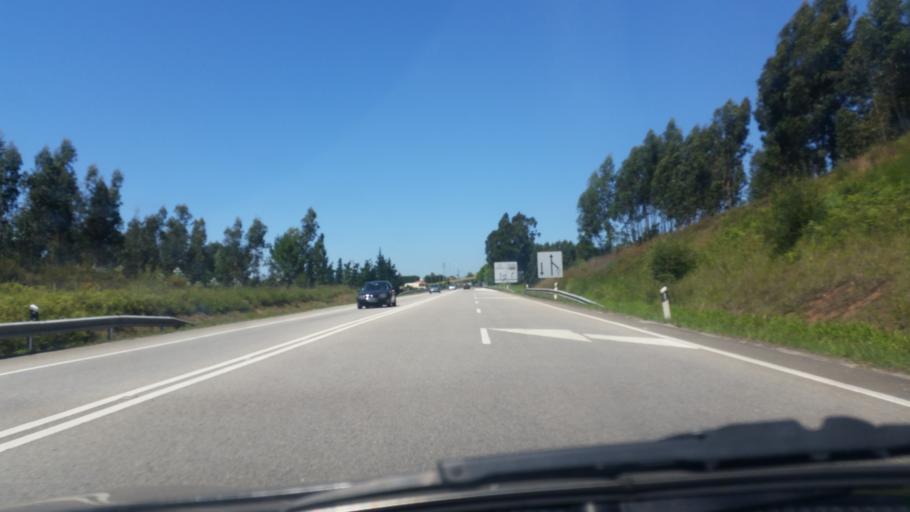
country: PT
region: Aveiro
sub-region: Agueda
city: Valongo
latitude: 40.6033
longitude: -8.4673
